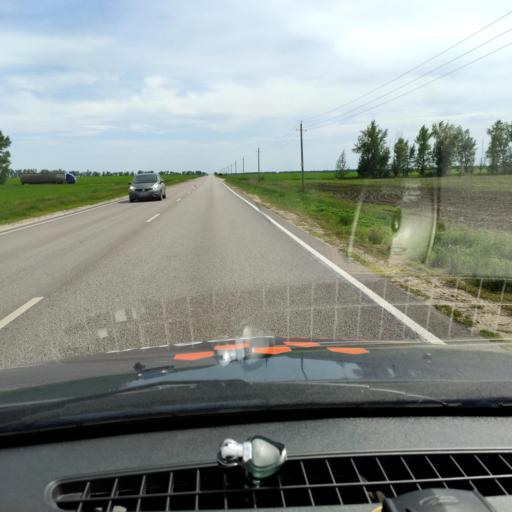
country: RU
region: Voronezj
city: Novaya Usman'
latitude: 51.5662
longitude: 39.3756
